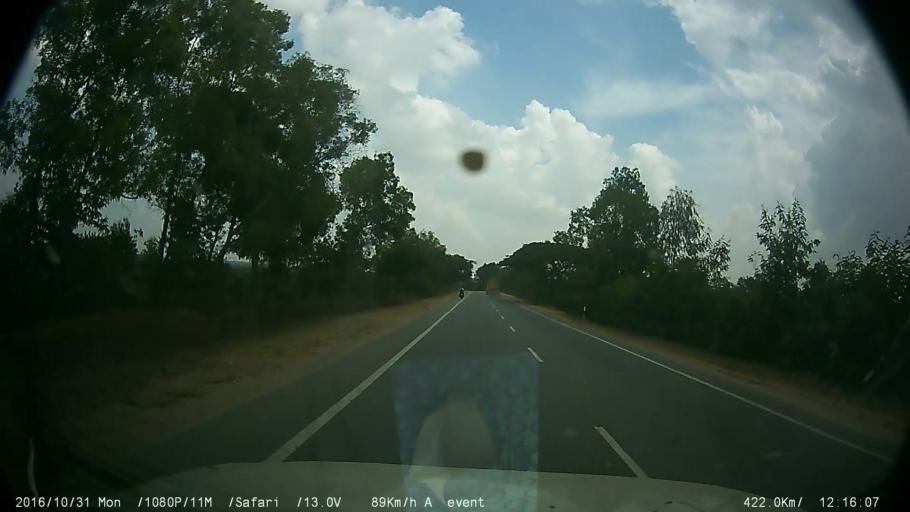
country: IN
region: Karnataka
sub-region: Mysore
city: Hunsur
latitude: 12.3359
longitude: 76.3848
